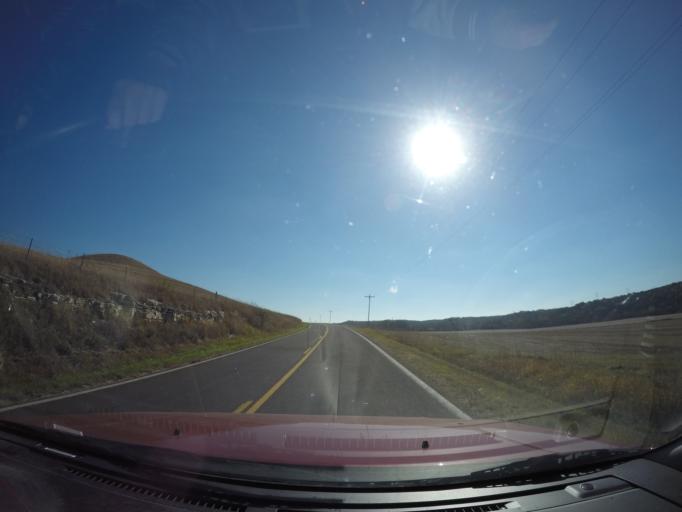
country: US
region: Kansas
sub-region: Geary County
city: Grandview Plaza
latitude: 38.9892
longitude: -96.7268
